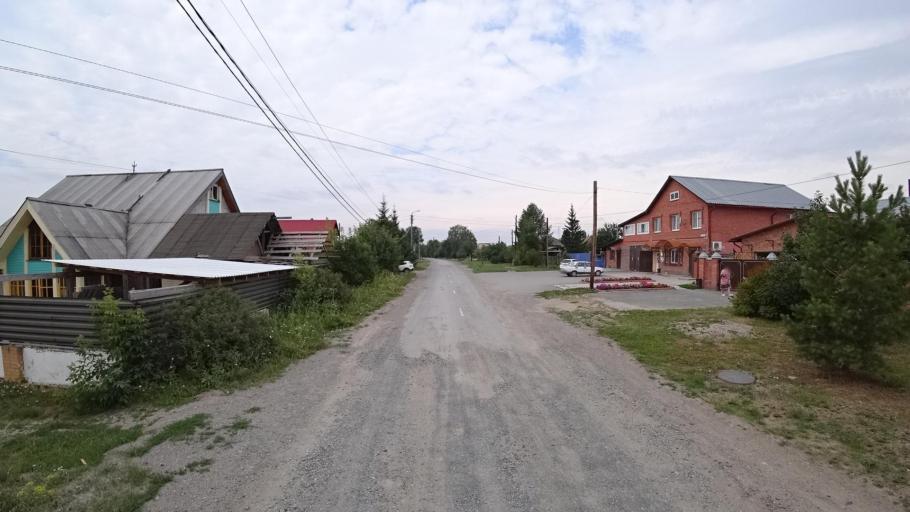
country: RU
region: Sverdlovsk
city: Kamyshlov
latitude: 56.8466
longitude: 62.7408
